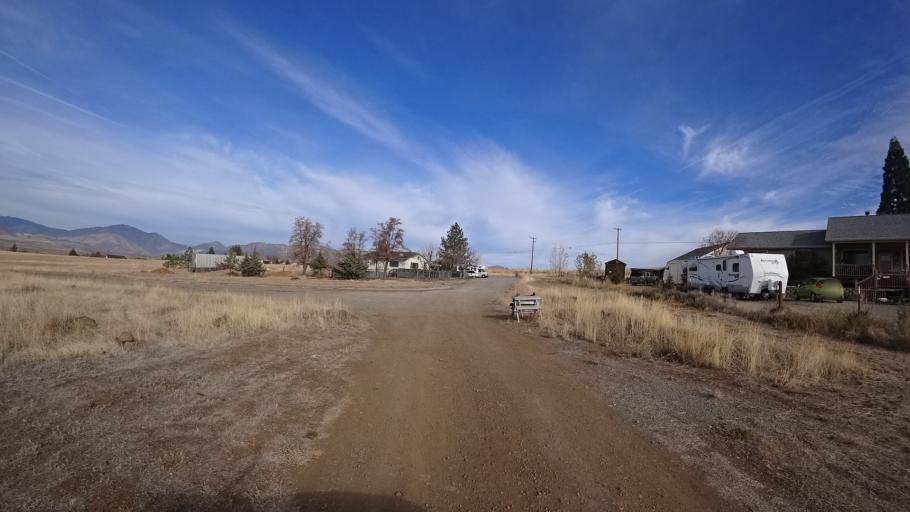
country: US
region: California
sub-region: Siskiyou County
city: Montague
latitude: 41.7299
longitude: -122.5155
